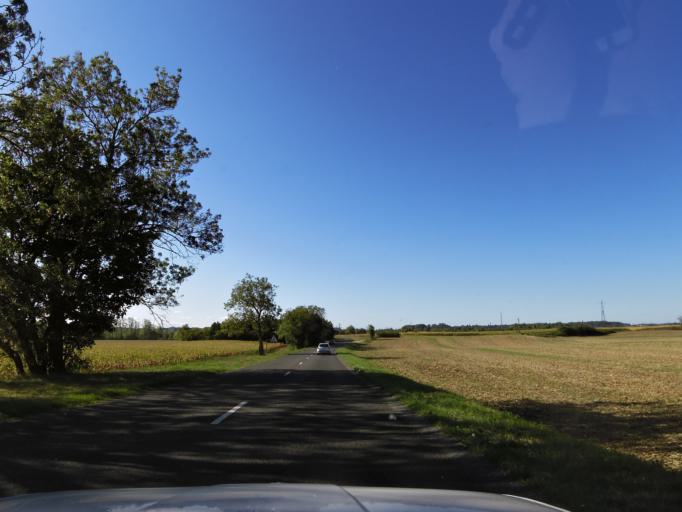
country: FR
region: Rhone-Alpes
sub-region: Departement de l'Ain
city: Chazey-sur-Ain
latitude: 45.9021
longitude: 5.2474
